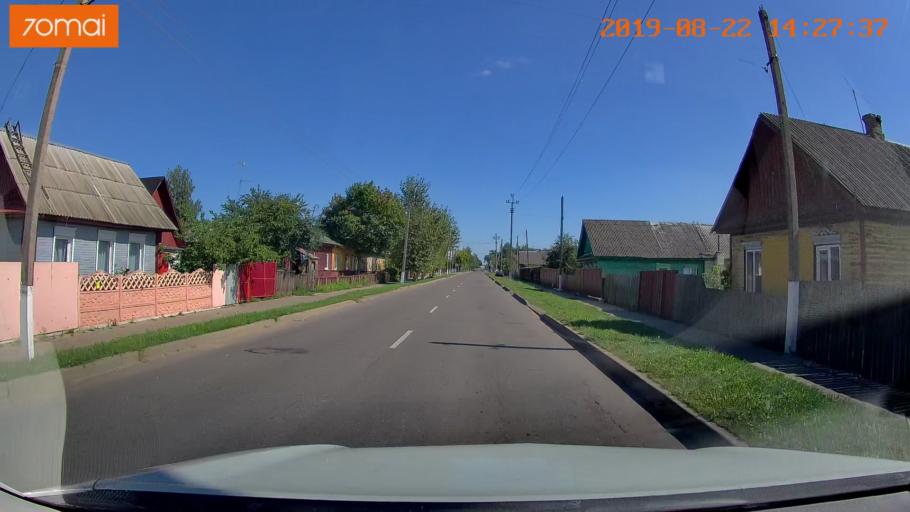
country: BY
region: Mogilev
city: Asipovichy
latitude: 53.2965
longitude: 28.6288
